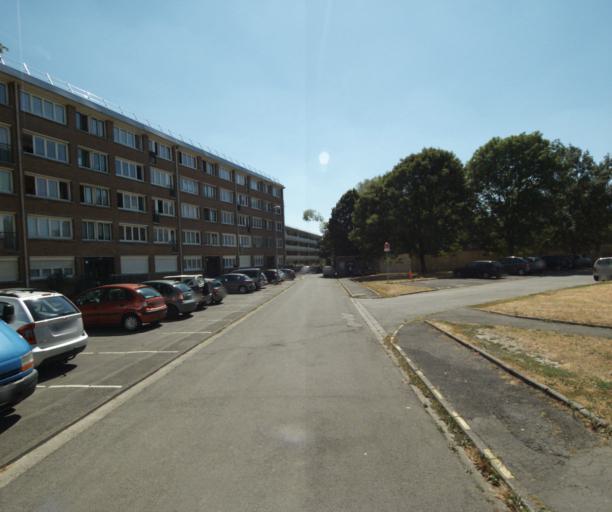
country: BE
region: Wallonia
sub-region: Province du Hainaut
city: Mouscron
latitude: 50.7334
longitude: 3.1850
